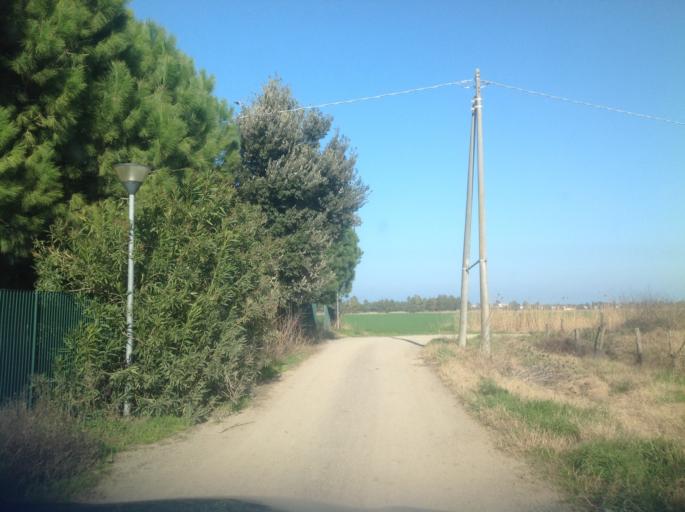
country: IT
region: Calabria
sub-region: Provincia di Cosenza
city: Sibari
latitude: 39.7216
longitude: 16.4957
